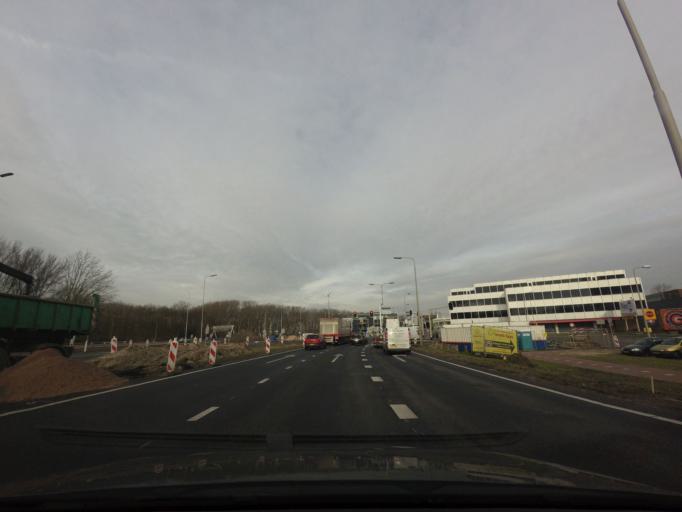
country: NL
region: North Holland
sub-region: Gemeente Beverwijk
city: Beverwijk
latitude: 52.4746
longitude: 4.6563
